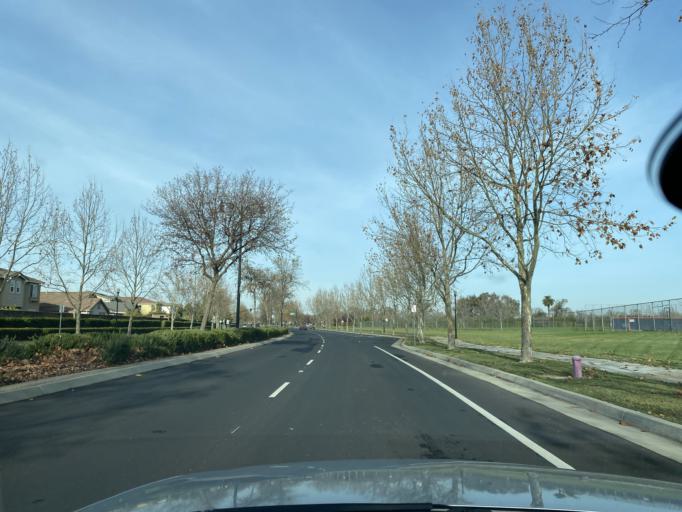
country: US
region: California
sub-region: Sacramento County
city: Elk Grove
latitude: 38.3988
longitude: -121.4001
